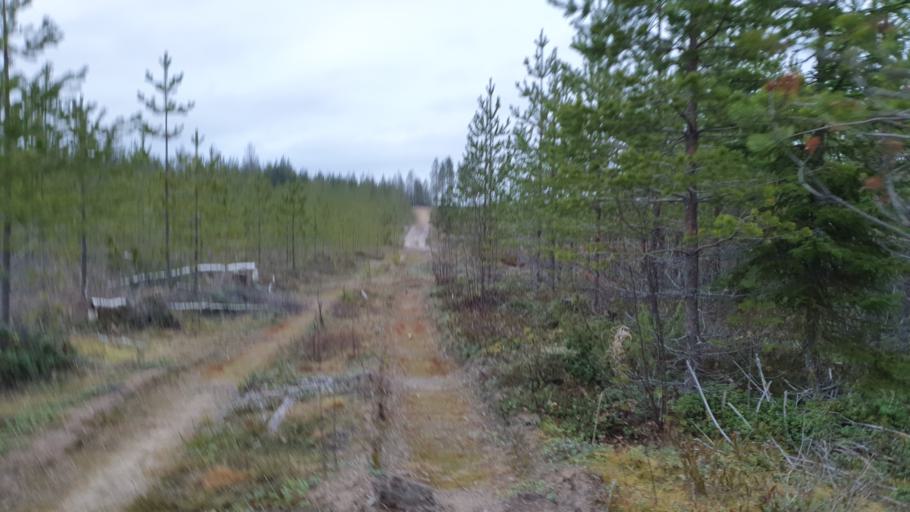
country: FI
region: Kainuu
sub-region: Kehys-Kainuu
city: Kuhmo
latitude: 64.1466
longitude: 29.4088
